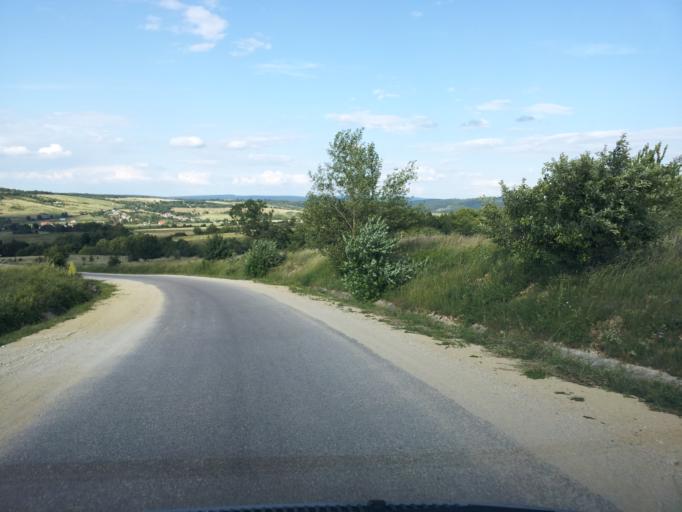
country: HU
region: Veszprem
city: Zirc
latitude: 47.1954
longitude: 17.8368
